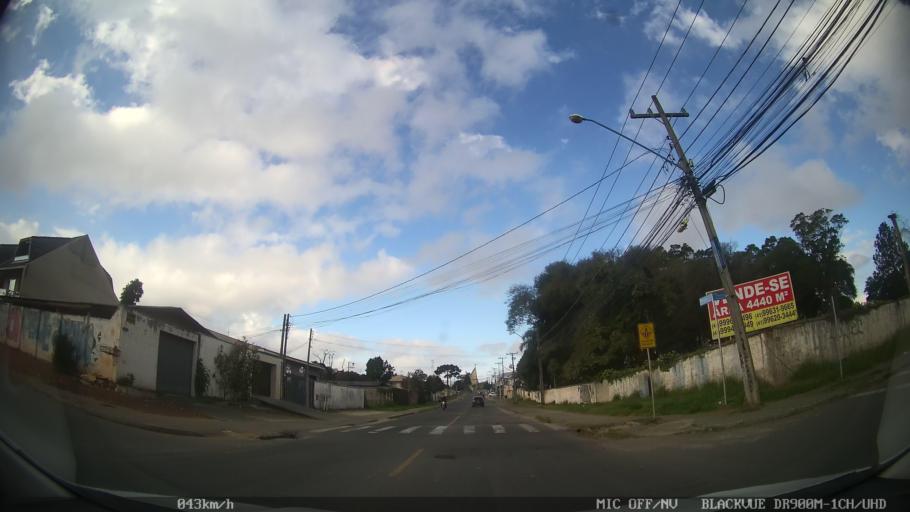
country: BR
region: Parana
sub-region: Pinhais
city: Pinhais
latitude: -25.4241
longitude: -49.1876
